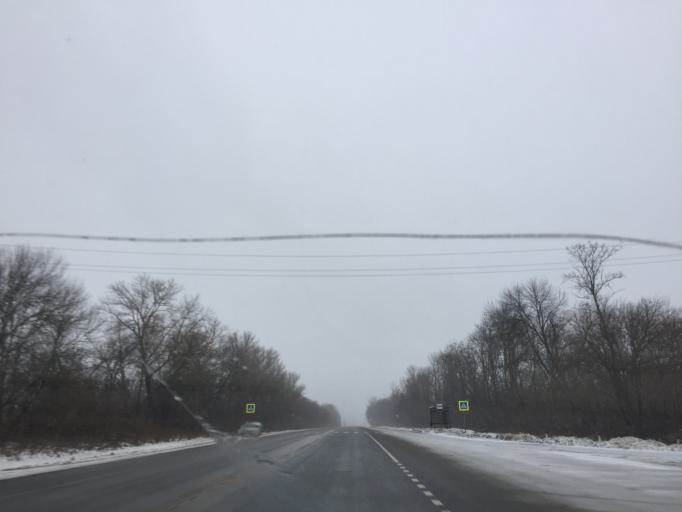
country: RU
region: Tula
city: Plavsk
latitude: 53.7326
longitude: 37.3090
